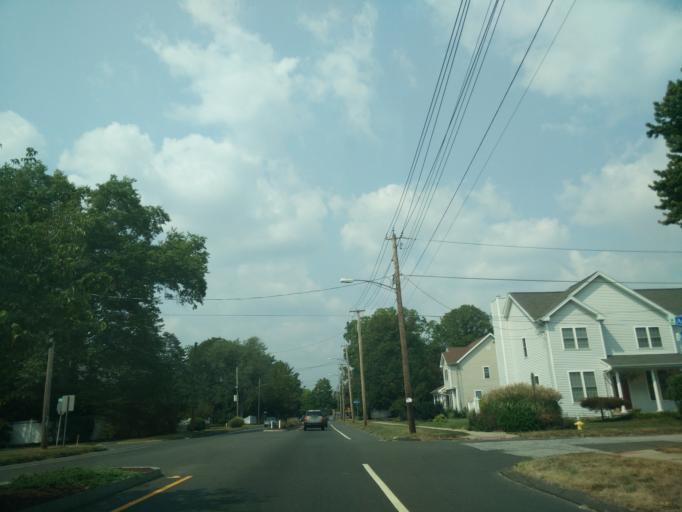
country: US
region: Connecticut
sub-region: Fairfield County
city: Bridgeport
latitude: 41.1850
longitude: -73.2188
